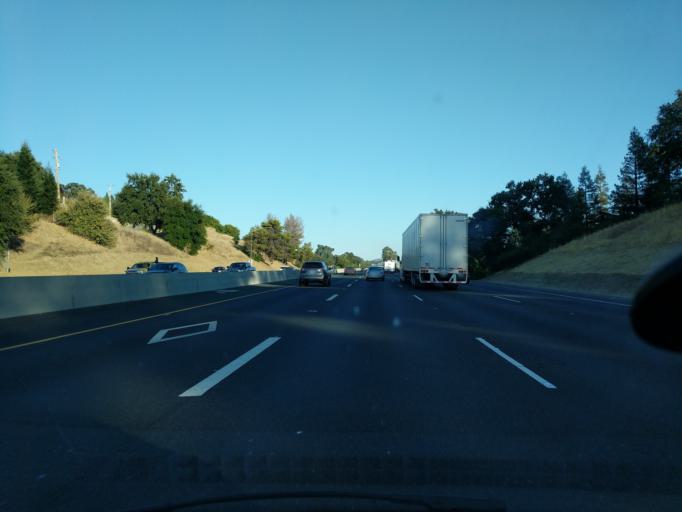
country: US
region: California
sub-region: Contra Costa County
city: Danville
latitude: 37.8377
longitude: -122.0139
